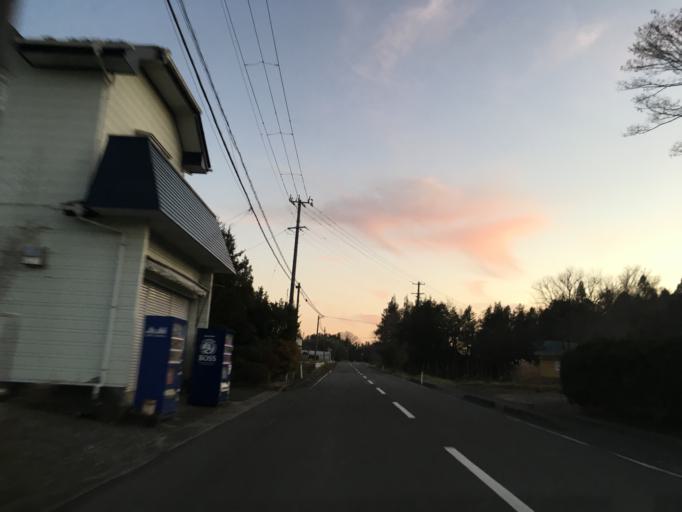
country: JP
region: Iwate
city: Ichinoseki
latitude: 38.7431
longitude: 141.2185
